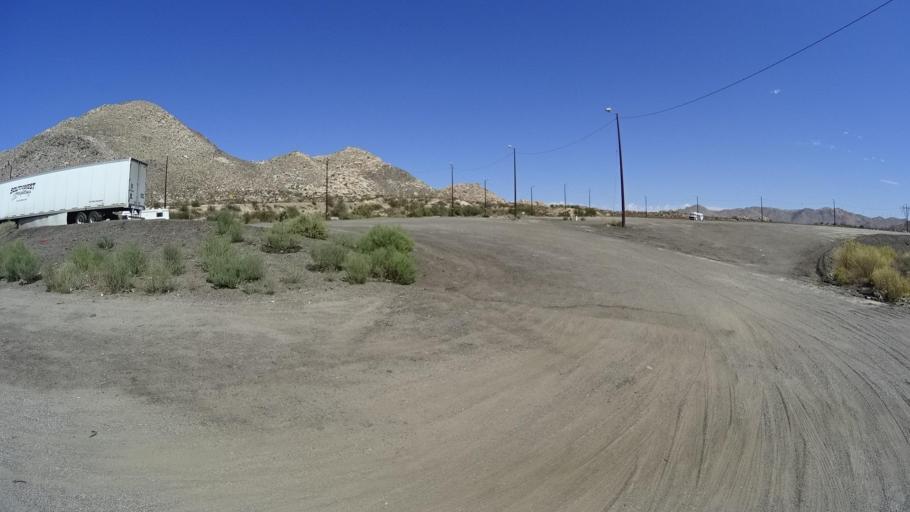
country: MX
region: Baja California
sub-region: Tecate
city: Cereso del Hongo
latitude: 32.6346
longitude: -116.1655
